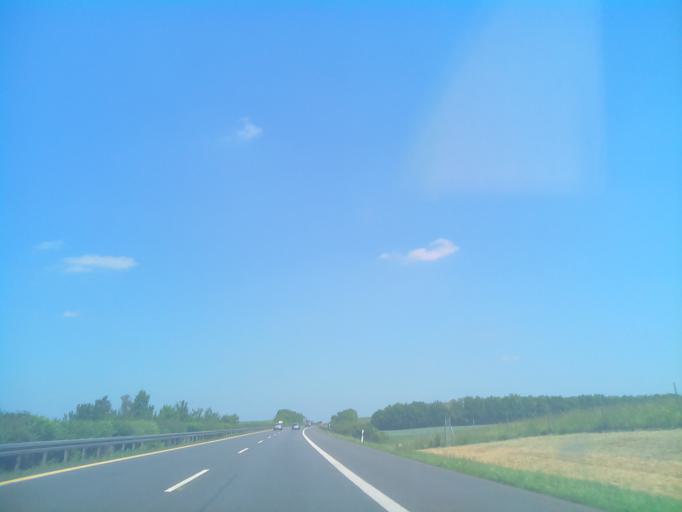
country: DE
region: Baden-Wuerttemberg
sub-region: Regierungsbezirk Stuttgart
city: Grossrinderfeld
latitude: 49.6349
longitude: 9.7305
